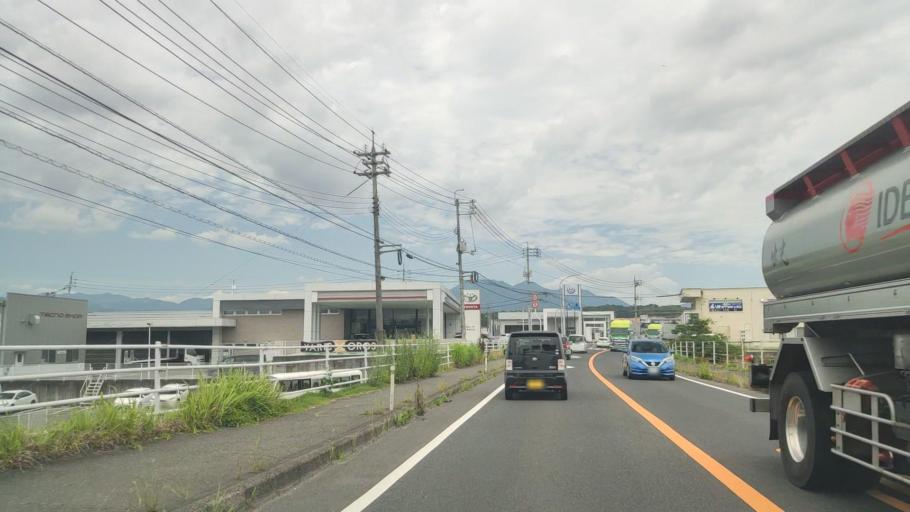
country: JP
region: Okayama
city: Tsuyama
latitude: 35.0686
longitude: 134.0509
